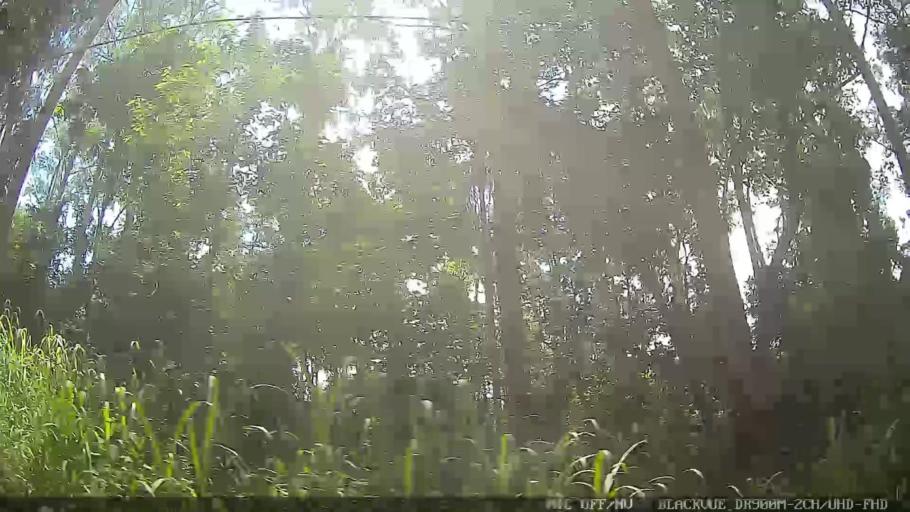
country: BR
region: Sao Paulo
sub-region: Atibaia
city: Atibaia
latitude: -23.1453
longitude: -46.6421
